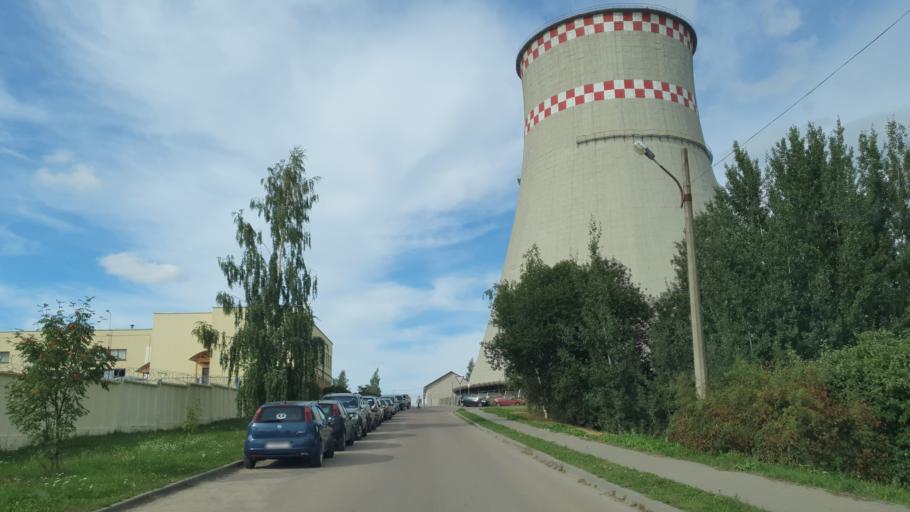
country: BY
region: Minsk
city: Azyartso
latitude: 53.8681
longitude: 27.3951
